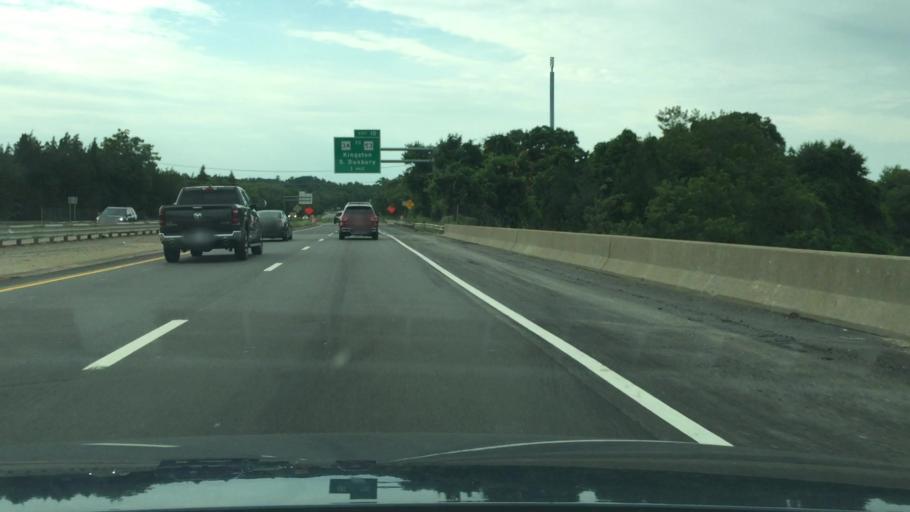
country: US
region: Massachusetts
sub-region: Plymouth County
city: Kingston
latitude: 41.9970
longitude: -70.7208
